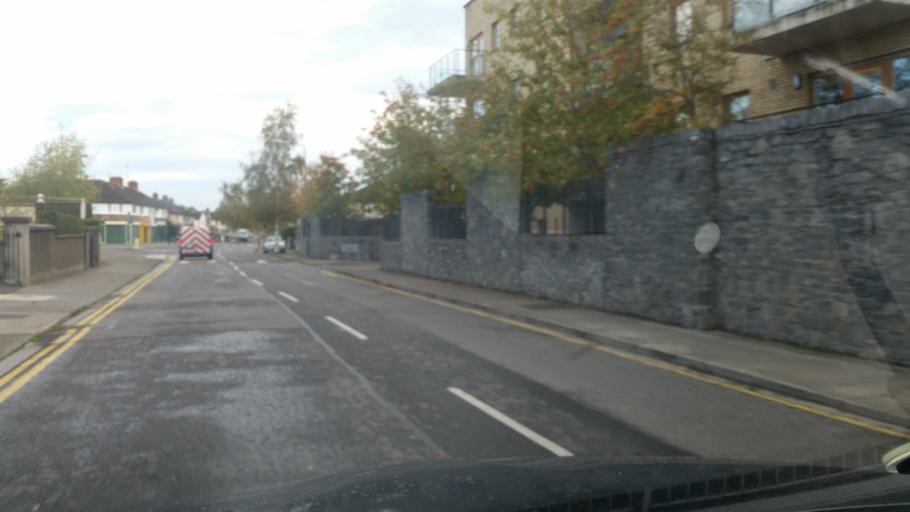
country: IE
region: Leinster
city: Cabra
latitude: 53.3584
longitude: -6.2878
